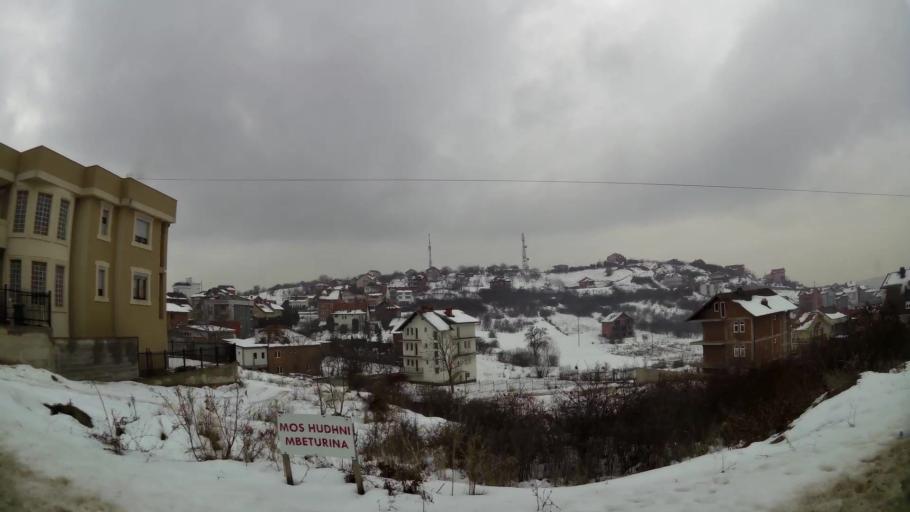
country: XK
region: Pristina
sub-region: Komuna e Prishtines
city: Pristina
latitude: 42.6741
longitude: 21.1855
